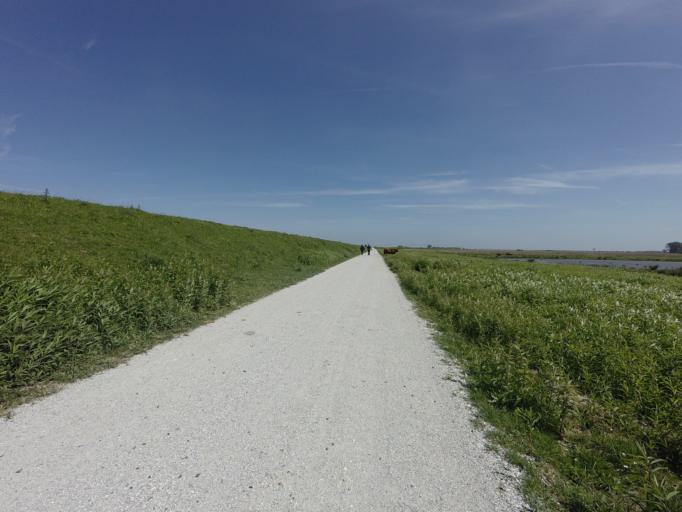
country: NL
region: South Holland
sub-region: Gemeente Spijkenisse
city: Spijkenisse
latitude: 51.7487
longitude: 4.2983
